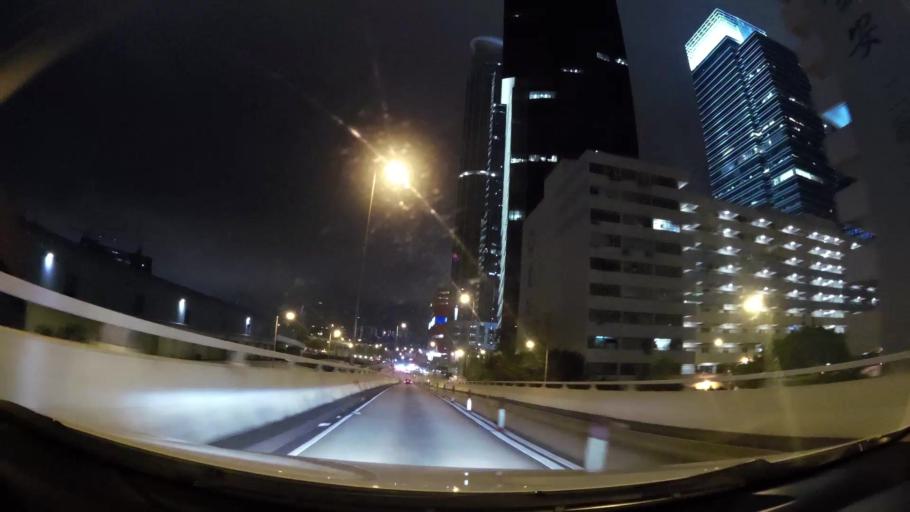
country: HK
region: Kowloon City
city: Kowloon
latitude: 22.3194
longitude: 114.2114
